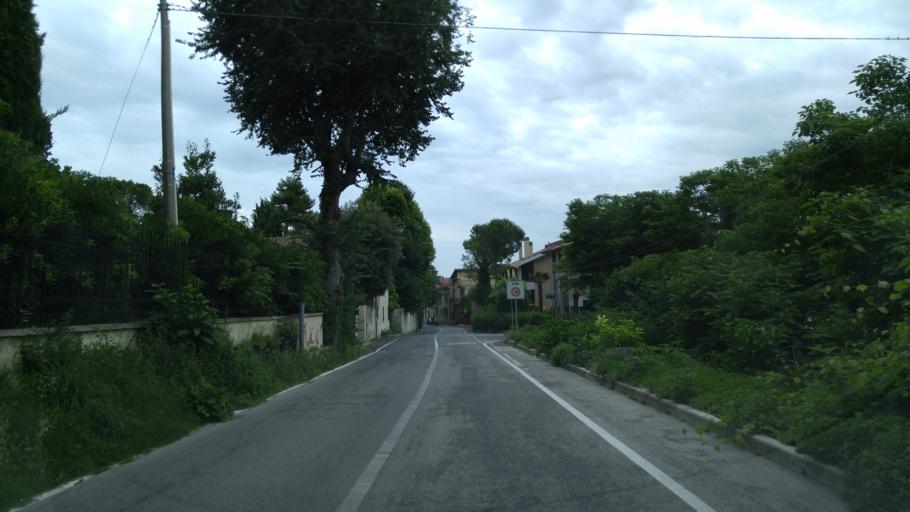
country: IT
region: The Marches
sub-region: Provincia di Pesaro e Urbino
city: Pesaro
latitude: 43.9132
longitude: 12.8964
